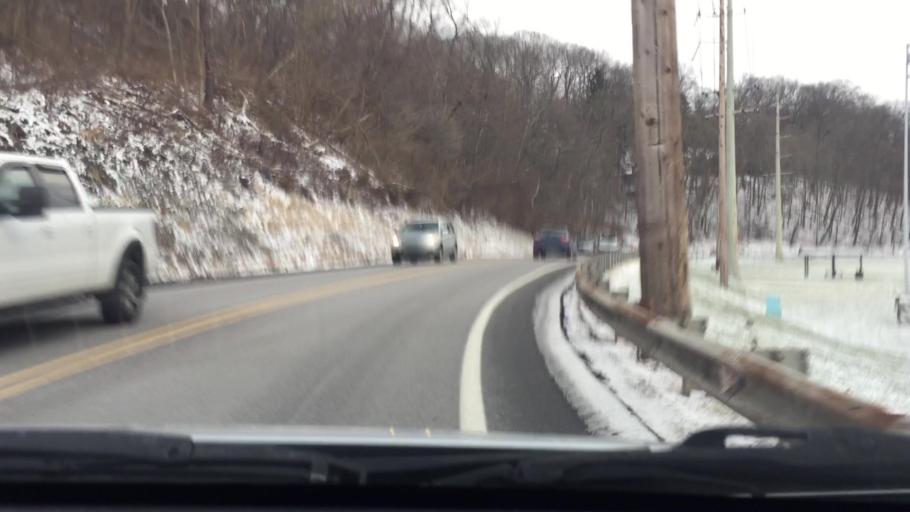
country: US
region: Pennsylvania
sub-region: Allegheny County
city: Upper Saint Clair
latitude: 40.3422
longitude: -80.0794
